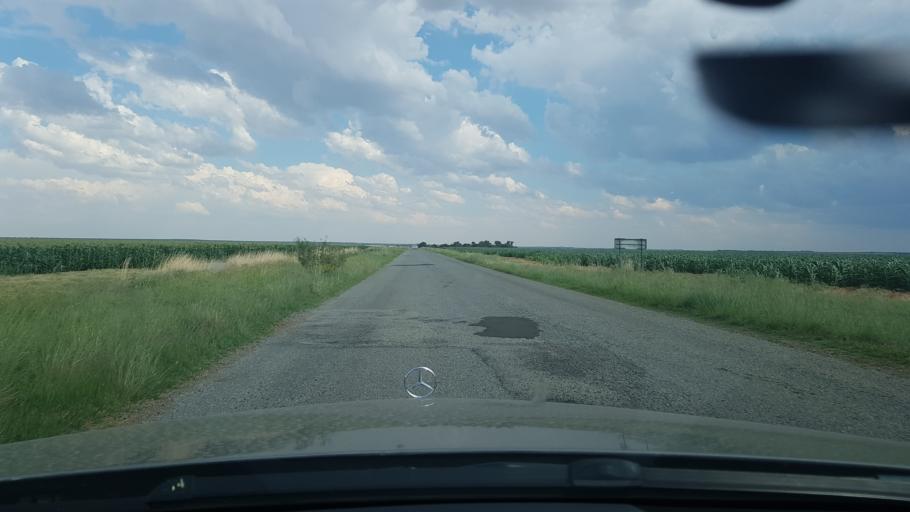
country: ZA
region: North-West
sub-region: Dr Ruth Segomotsi Mompati District Municipality
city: Bloemhof
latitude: -27.8213
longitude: 25.6312
